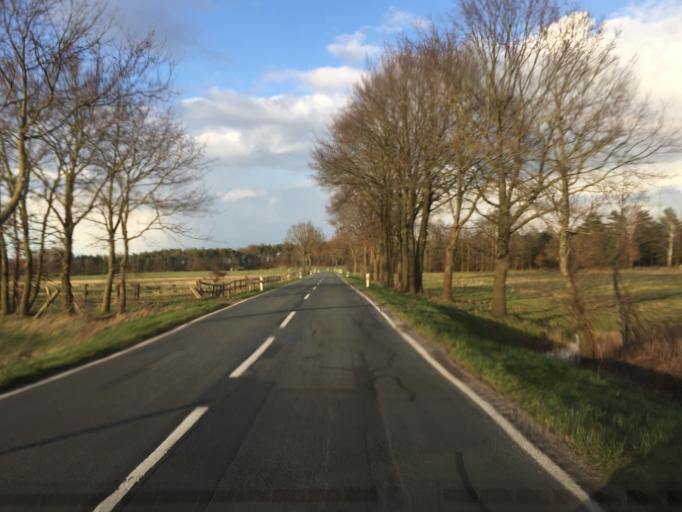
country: DE
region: Lower Saxony
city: Steyerberg
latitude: 52.5821
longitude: 8.9772
